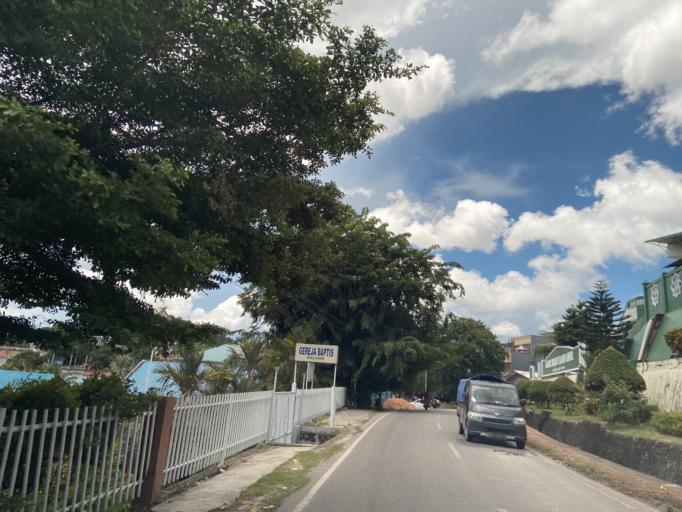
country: SG
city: Singapore
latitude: 1.1380
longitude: 104.0120
